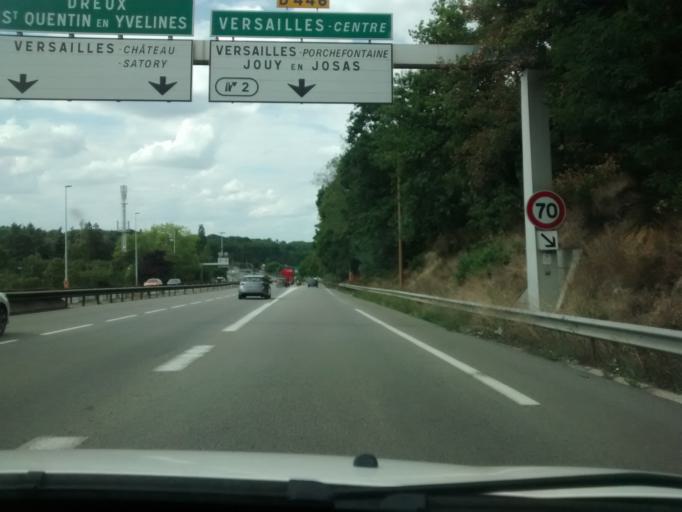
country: FR
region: Ile-de-France
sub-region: Departement des Yvelines
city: Viroflay
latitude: 48.7846
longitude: 2.1565
